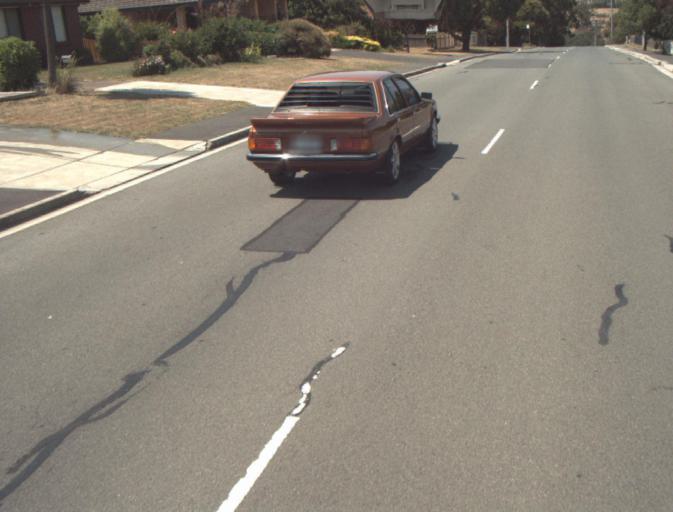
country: AU
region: Tasmania
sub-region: Launceston
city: Newstead
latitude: -41.4703
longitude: 147.1789
